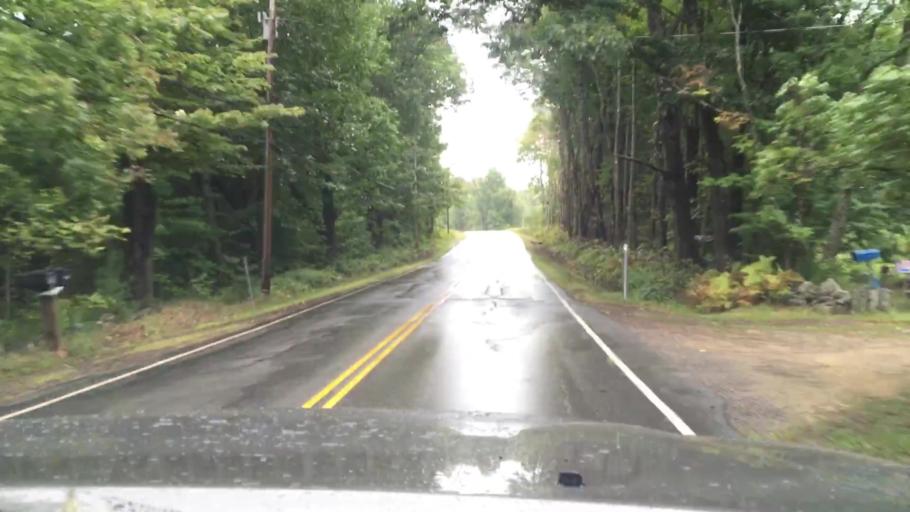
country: US
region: New Hampshire
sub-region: Belknap County
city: Meredith
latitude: 43.6542
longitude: -71.5491
